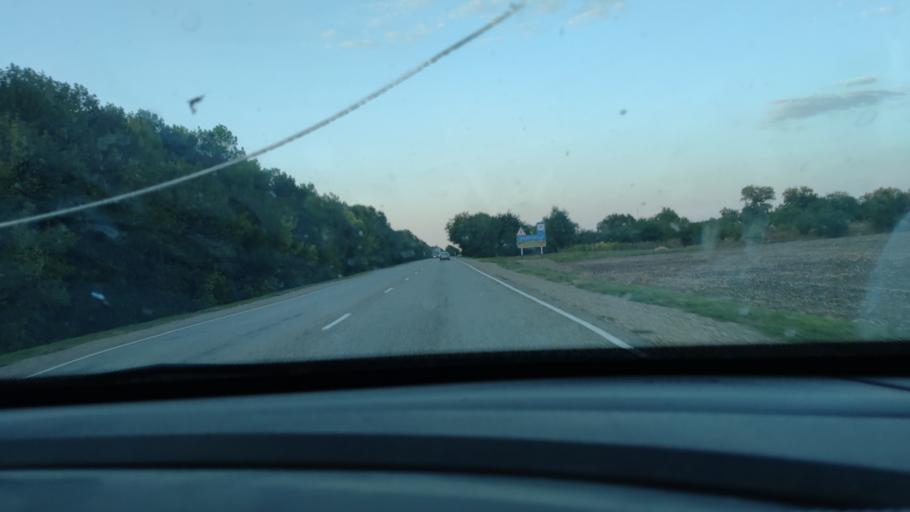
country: RU
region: Krasnodarskiy
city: Novominskaya
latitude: 46.4083
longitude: 39.0023
